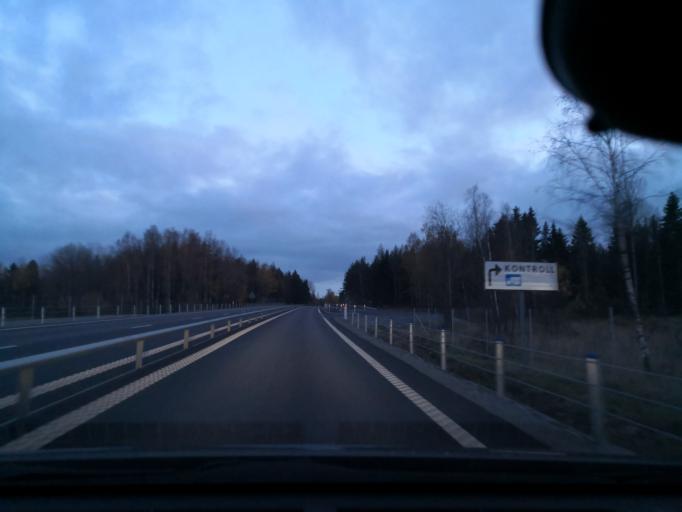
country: SE
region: Uppsala
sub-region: Enkopings Kommun
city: Enkoping
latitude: 59.6655
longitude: 17.0706
